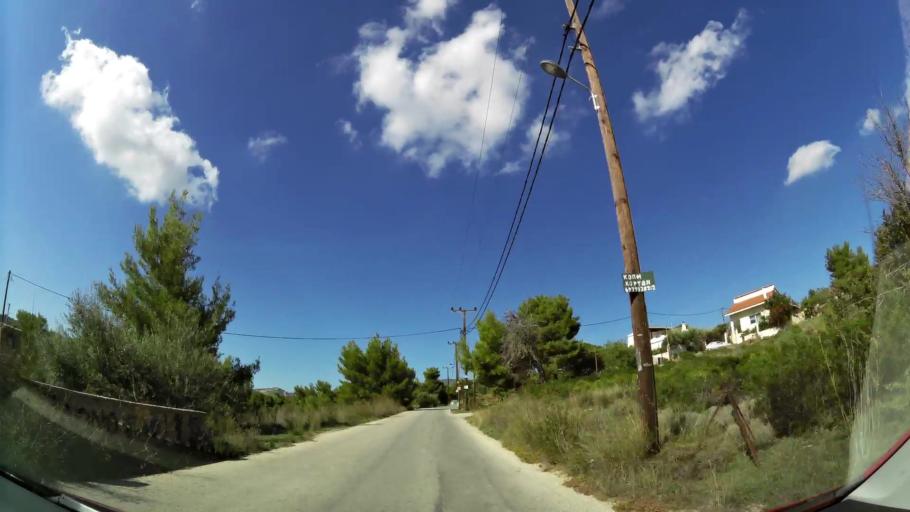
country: GR
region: Attica
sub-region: Nomarchia Anatolikis Attikis
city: Dioni
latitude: 38.0154
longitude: 23.9338
